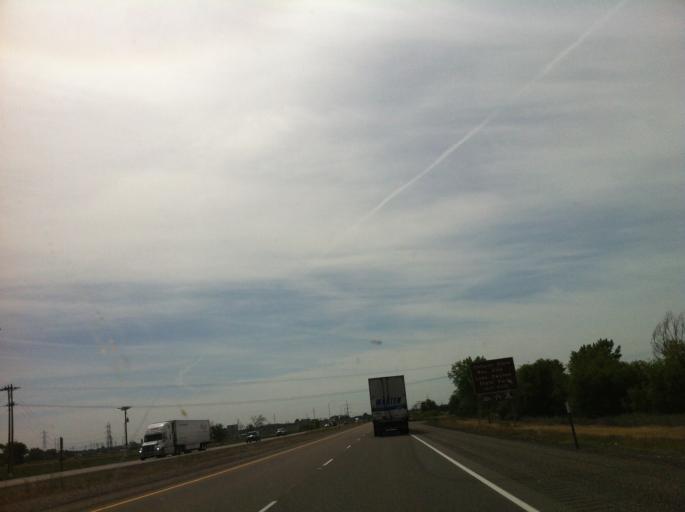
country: US
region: Oregon
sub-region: Malheur County
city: Ontario
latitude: 44.0581
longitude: -116.9887
